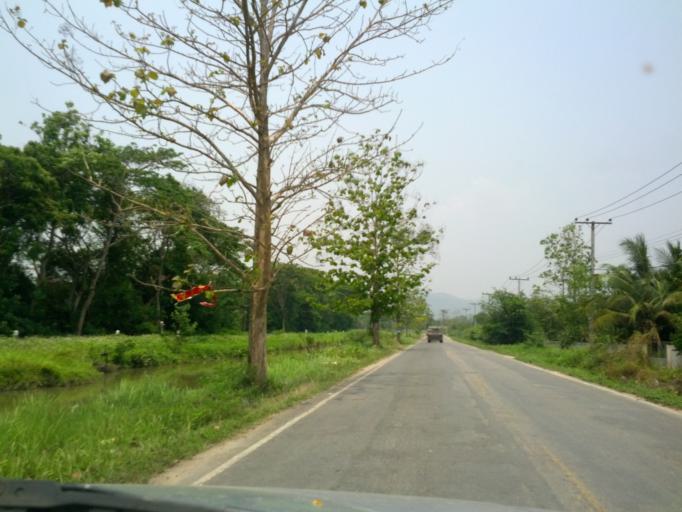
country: TH
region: Chiang Mai
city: San Sai
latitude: 18.8868
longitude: 99.0818
